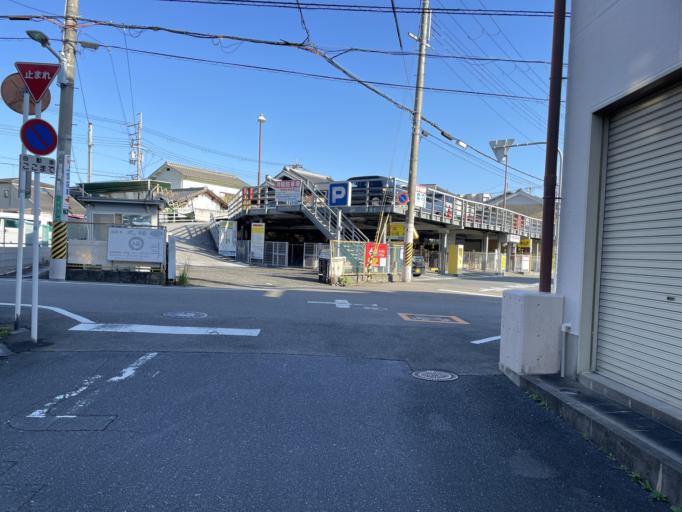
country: JP
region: Osaka
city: Tondabayashicho
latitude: 34.4524
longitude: 135.5710
